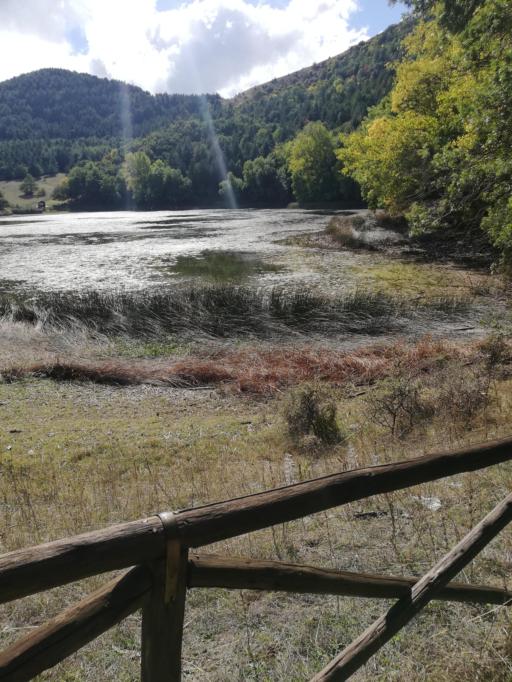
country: IT
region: Apulia
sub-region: Provincia di Foggia
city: Biccari
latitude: 41.3719
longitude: 15.1709
